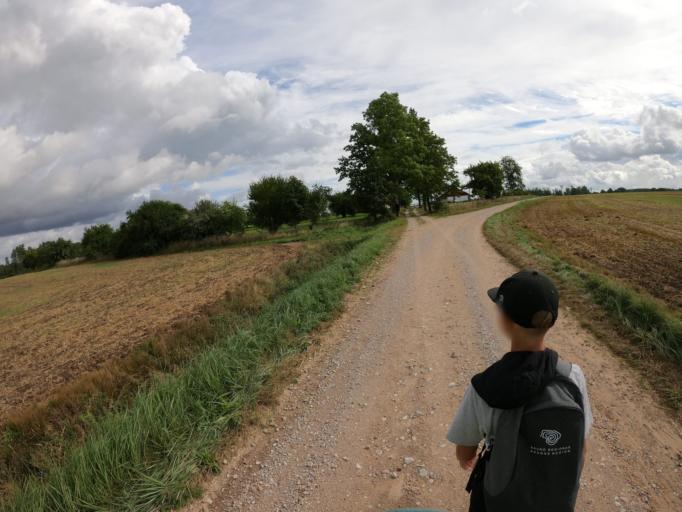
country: LV
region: Aizpute
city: Aizpute
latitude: 56.7080
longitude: 21.6788
